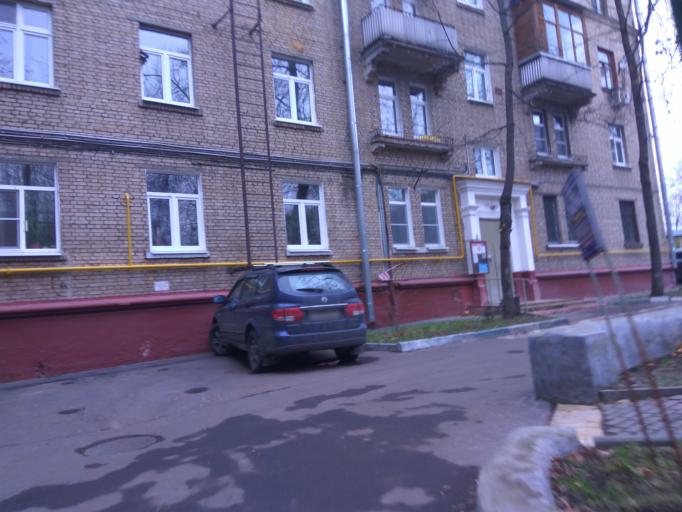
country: RU
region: Moscow
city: Kolomenskoye
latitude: 55.6443
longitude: 37.6719
